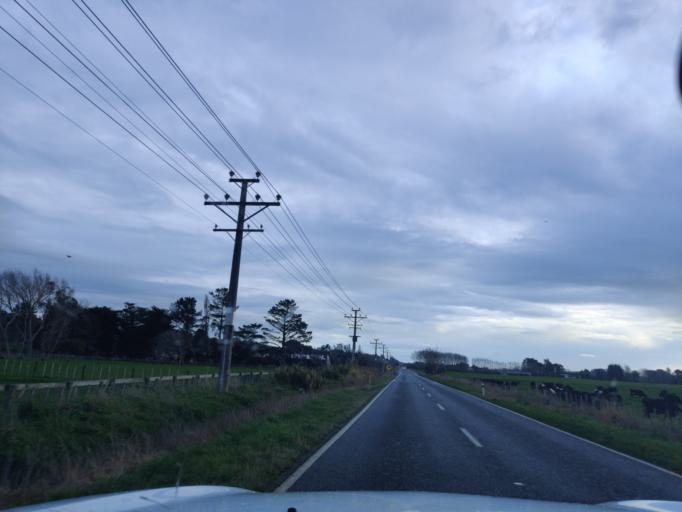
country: NZ
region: Manawatu-Wanganui
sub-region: Palmerston North City
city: Palmerston North
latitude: -40.3501
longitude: 175.6992
